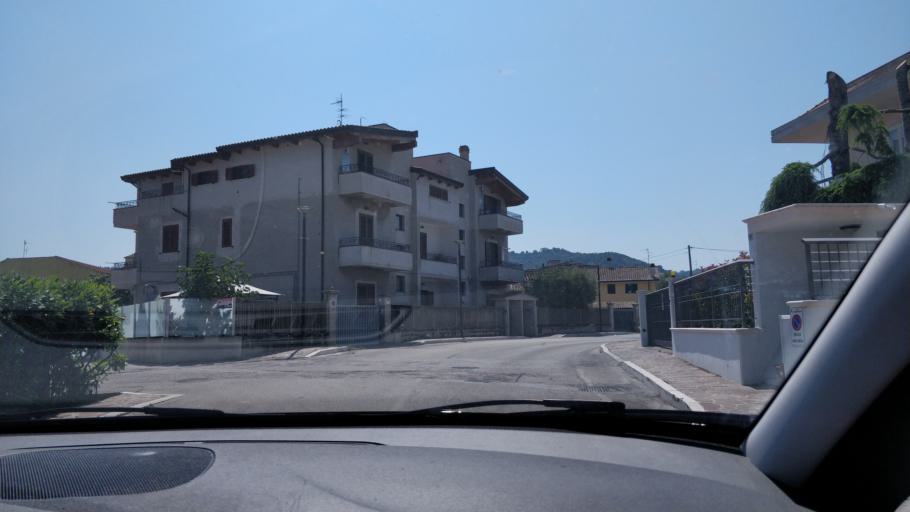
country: IT
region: Abruzzo
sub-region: Provincia di Chieti
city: Sambuceto
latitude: 42.4202
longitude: 14.1791
